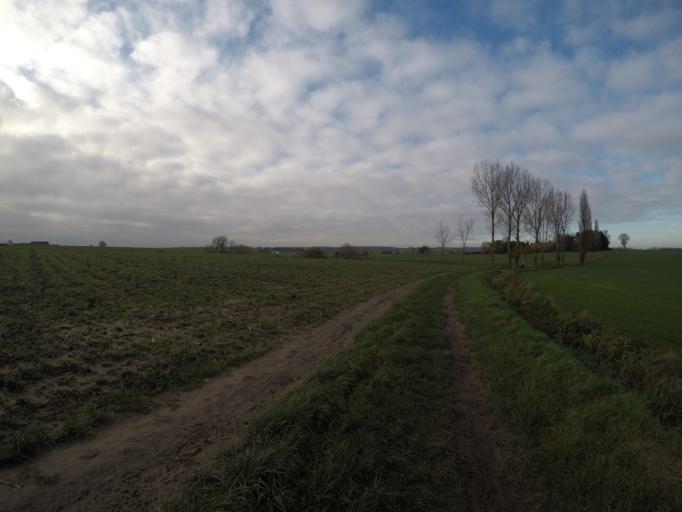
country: BE
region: Flanders
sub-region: Provincie West-Vlaanderen
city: Wervik
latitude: 50.8180
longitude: 3.0121
